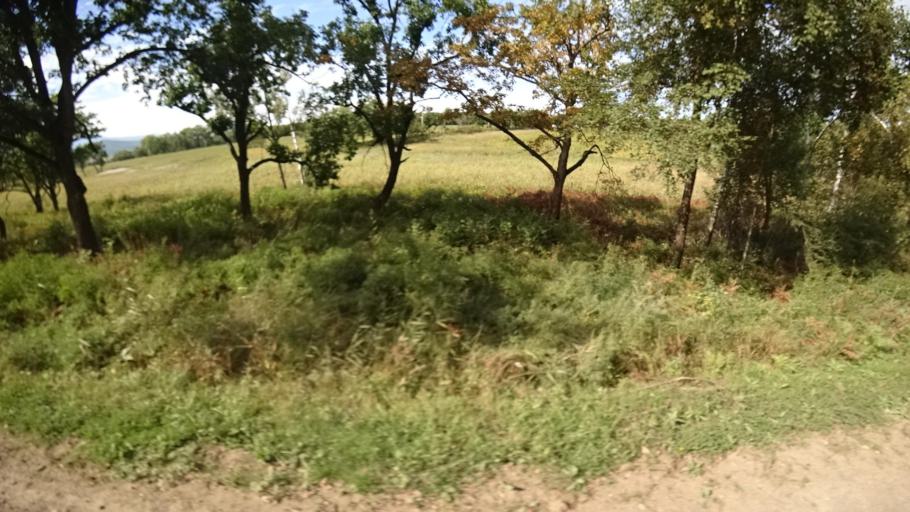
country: RU
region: Primorskiy
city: Dostoyevka
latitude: 44.3755
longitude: 133.5316
